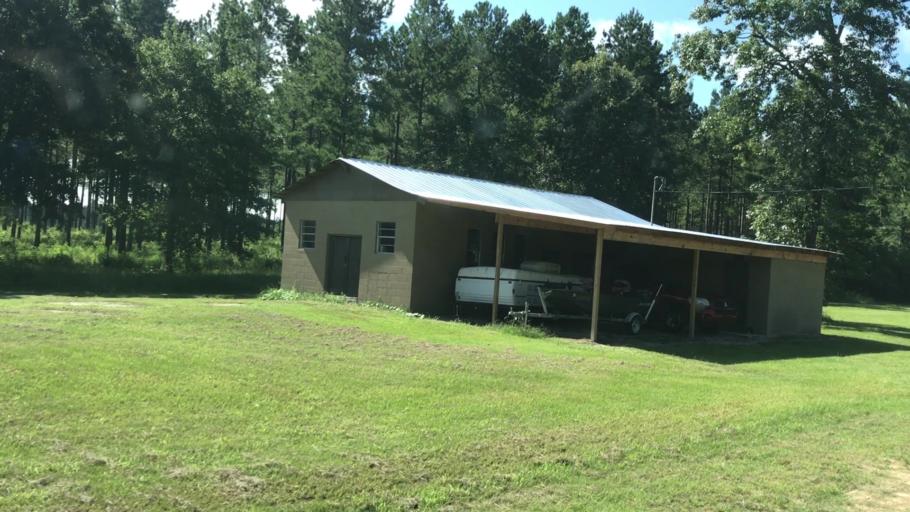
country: US
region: Georgia
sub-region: Jefferson County
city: Wadley
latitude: 32.8169
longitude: -82.3328
